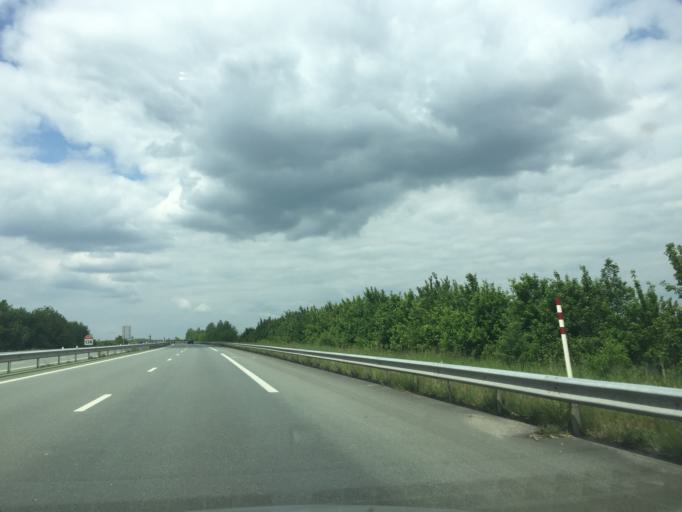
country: FR
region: Poitou-Charentes
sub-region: Departement des Deux-Sevres
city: Saint-Gelais
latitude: 46.4067
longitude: -0.3866
